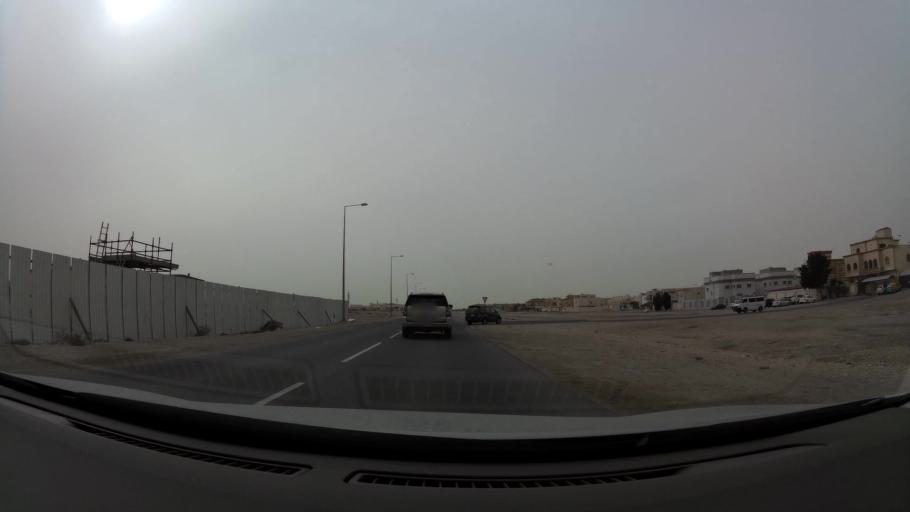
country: QA
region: Baladiyat ad Dawhah
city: Doha
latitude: 25.2399
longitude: 51.5162
